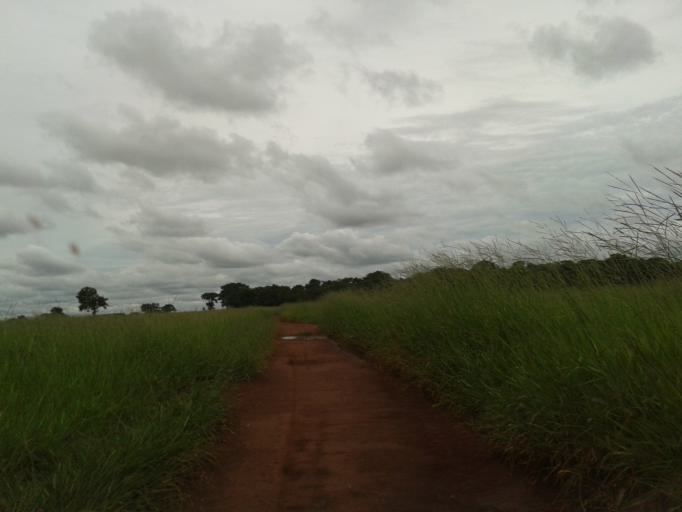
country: BR
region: Minas Gerais
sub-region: Capinopolis
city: Capinopolis
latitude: -18.7840
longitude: -49.7808
